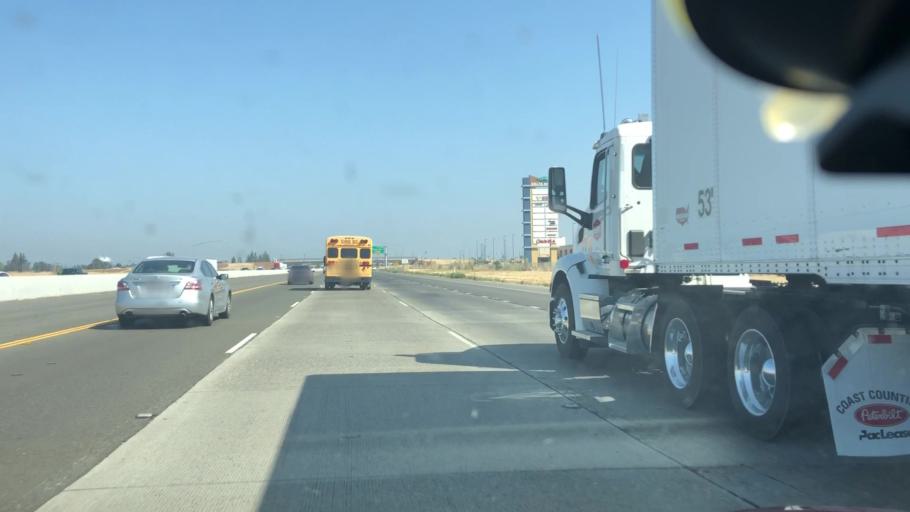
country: US
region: California
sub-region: Sacramento County
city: Parkway
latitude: 38.4597
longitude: -121.4946
